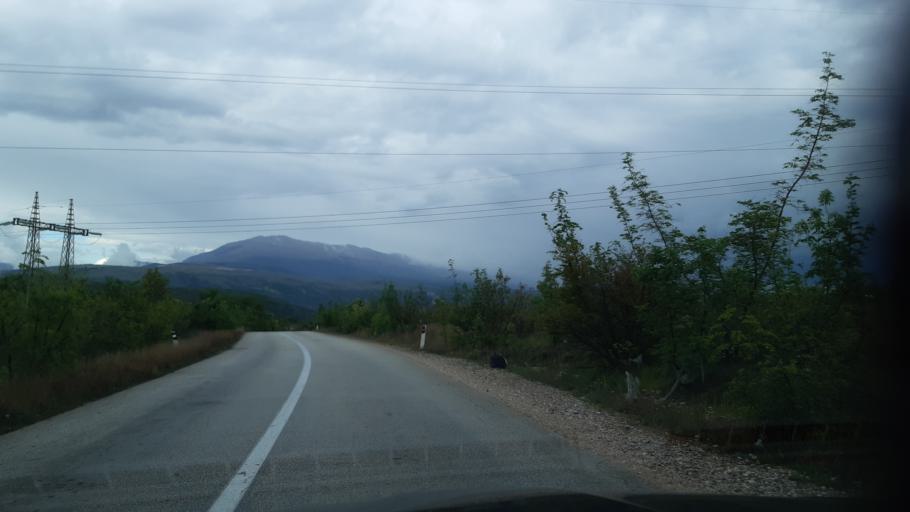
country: BA
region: Federation of Bosnia and Herzegovina
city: Rodoc
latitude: 43.3104
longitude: 17.7754
